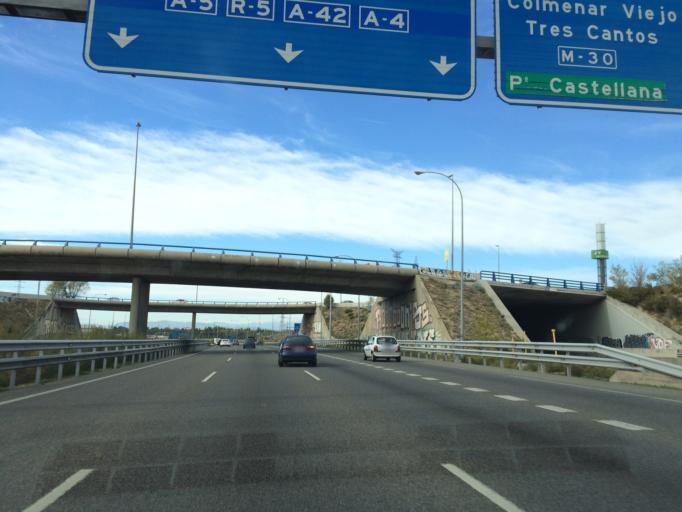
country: ES
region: Madrid
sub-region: Provincia de Madrid
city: Las Tablas
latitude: 40.5155
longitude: -3.6696
